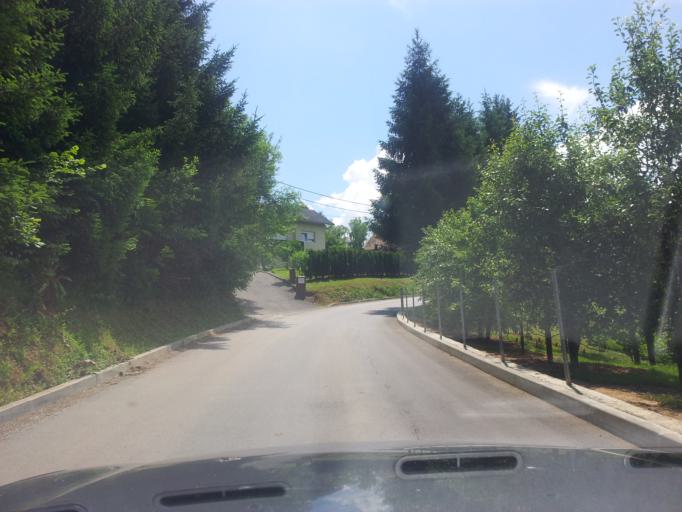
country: HR
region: Karlovacka
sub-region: Grad Karlovac
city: Karlovac
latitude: 45.4583
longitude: 15.5222
